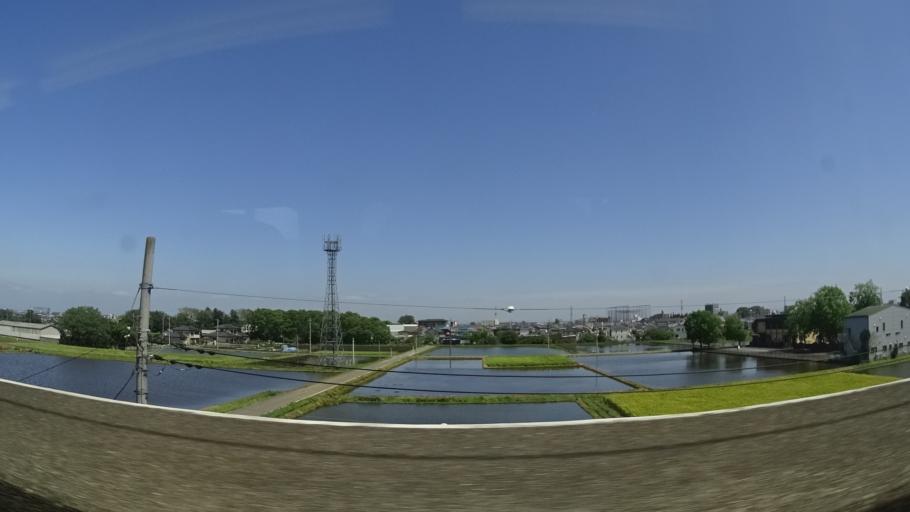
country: JP
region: Tochigi
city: Utsunomiya-shi
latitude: 36.5794
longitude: 139.9026
